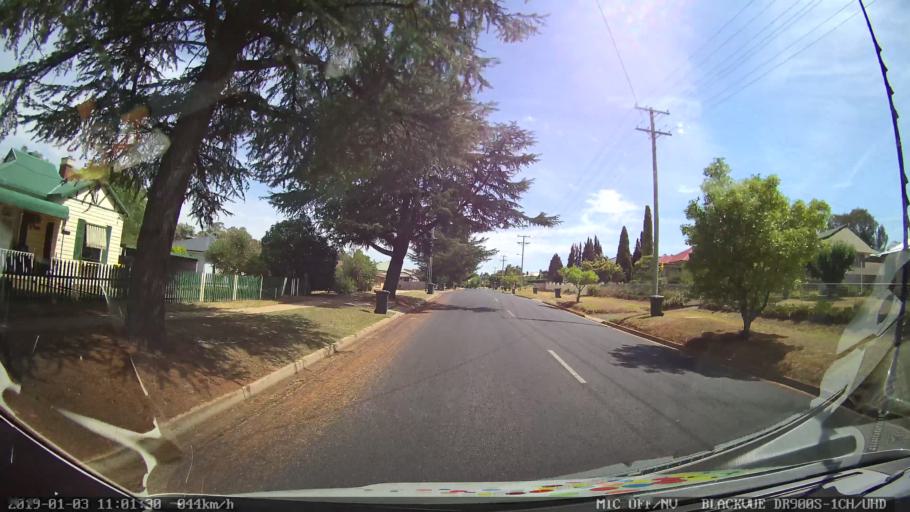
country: AU
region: New South Wales
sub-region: Young
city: Young
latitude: -34.3050
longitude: 148.2994
